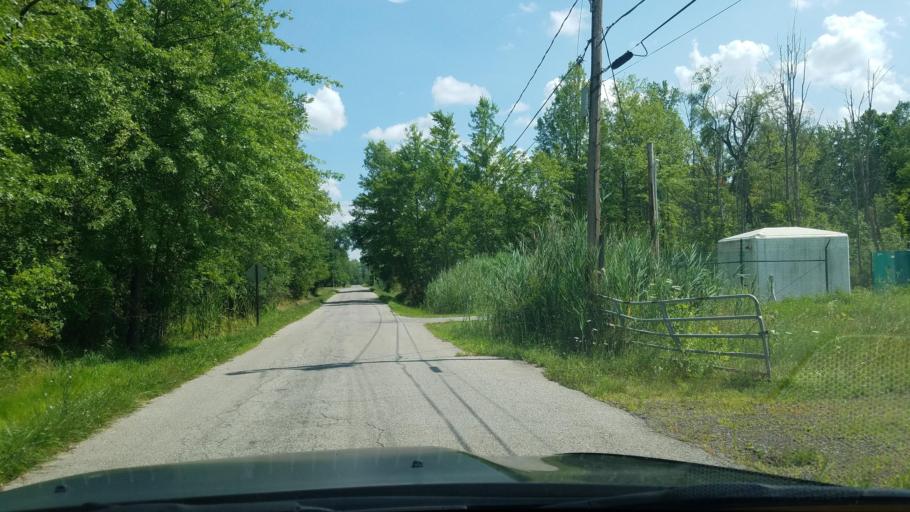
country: US
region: Ohio
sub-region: Trumbull County
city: Bolindale
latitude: 41.2072
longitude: -80.7903
